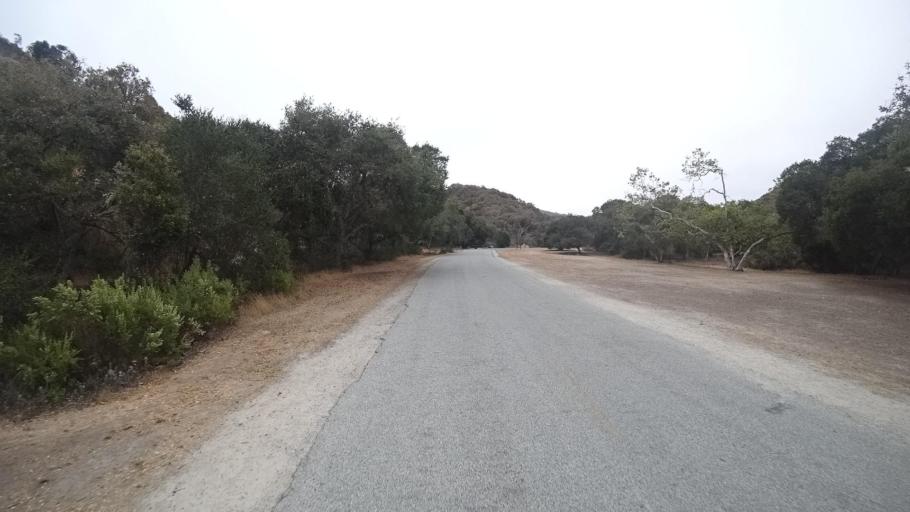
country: US
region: California
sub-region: Monterey County
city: Salinas
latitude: 36.5944
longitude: -121.6921
